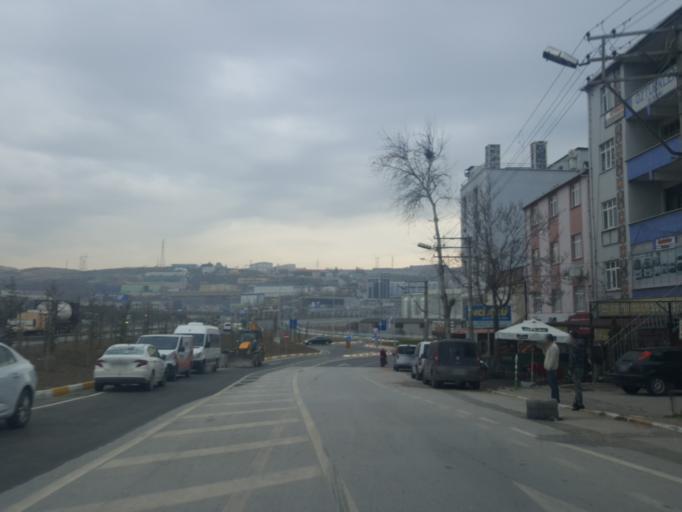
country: TR
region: Kocaeli
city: Tavsanli
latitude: 40.7886
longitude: 29.5321
